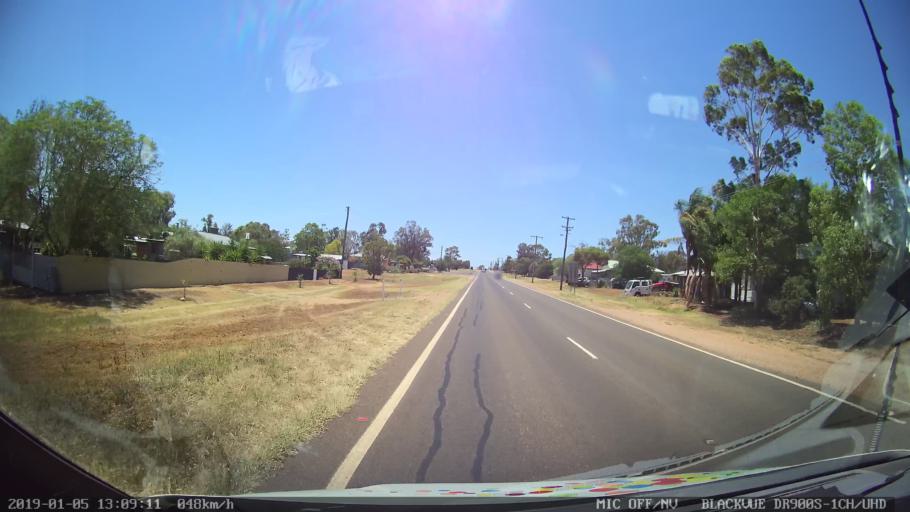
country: AU
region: New South Wales
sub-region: Gunnedah
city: Gunnedah
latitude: -31.0986
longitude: 149.9084
